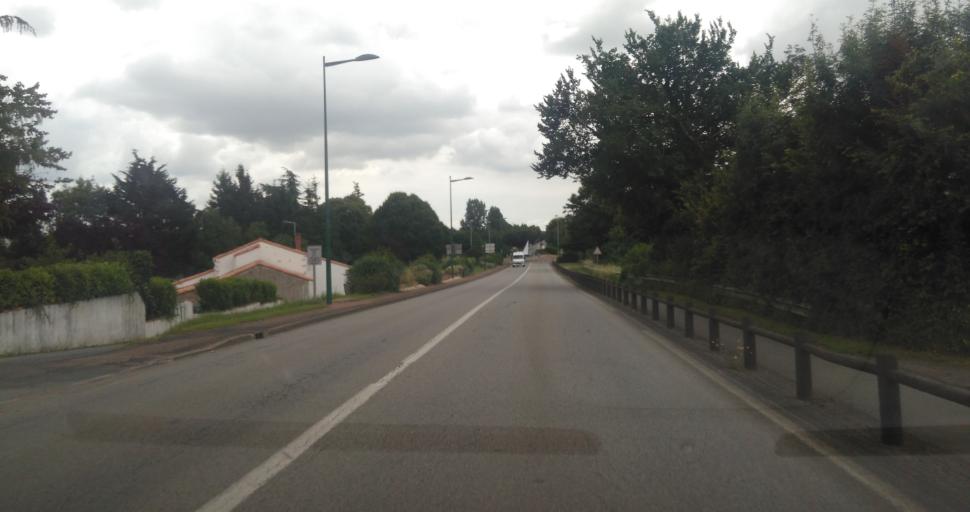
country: FR
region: Pays de la Loire
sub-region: Departement de la Vendee
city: Sainte-Hermine
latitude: 46.5534
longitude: -1.0622
